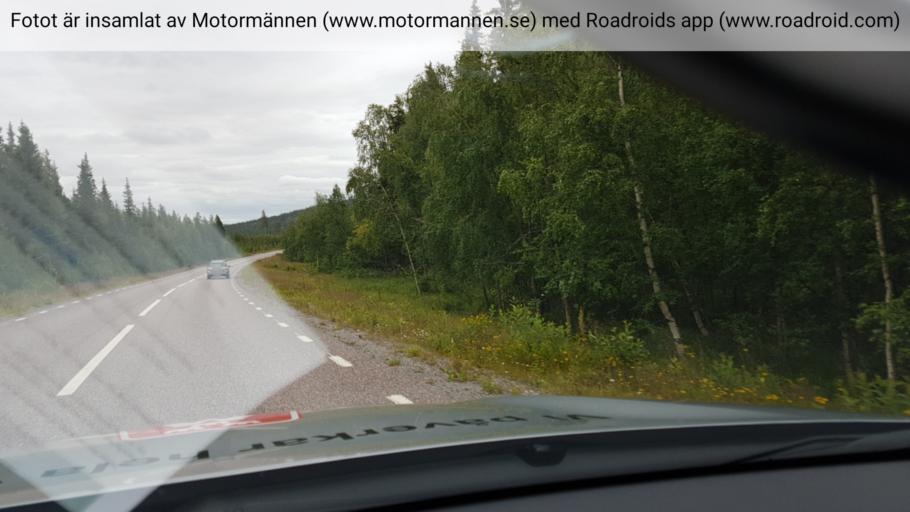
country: SE
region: Norrbotten
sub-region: Gallivare Kommun
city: Gaellivare
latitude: 67.0339
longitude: 21.7028
